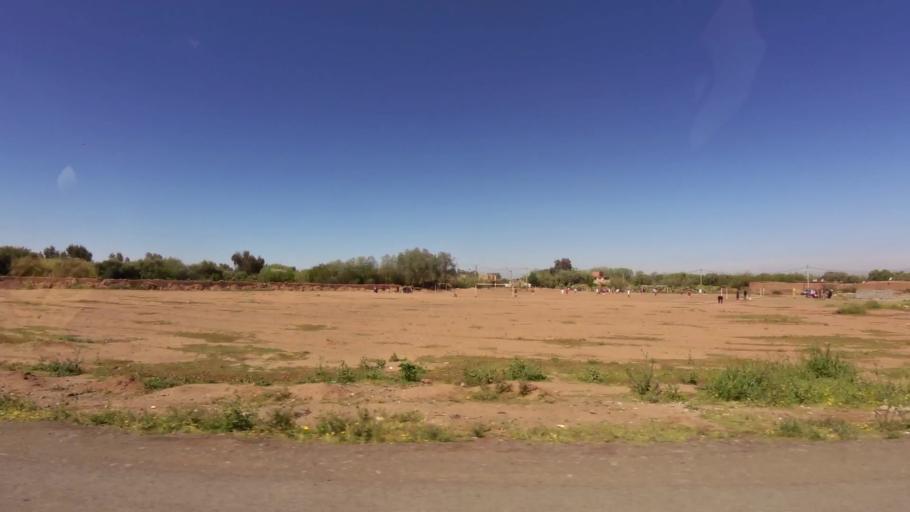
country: MA
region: Marrakech-Tensift-Al Haouz
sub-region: Marrakech
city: Marrakesh
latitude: 31.5854
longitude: -8.0619
